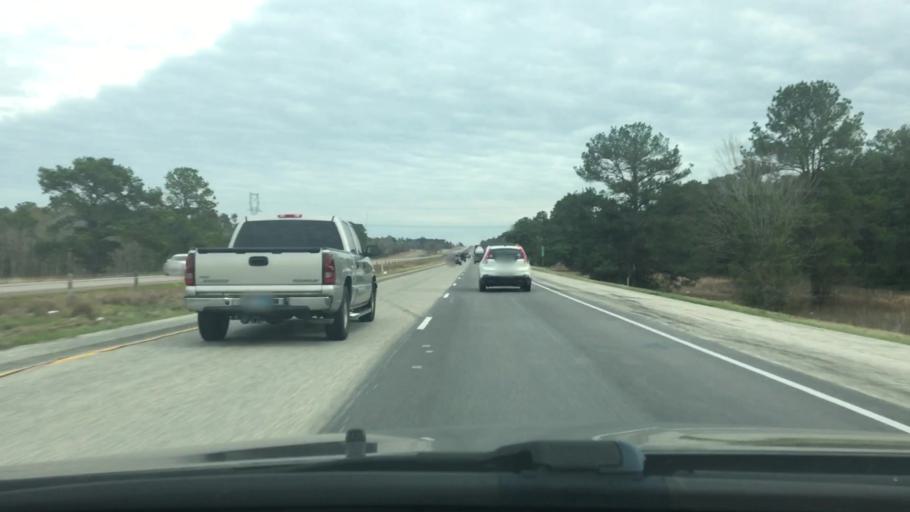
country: US
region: Texas
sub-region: Walker County
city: Huntsville
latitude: 30.7928
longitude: -95.6745
